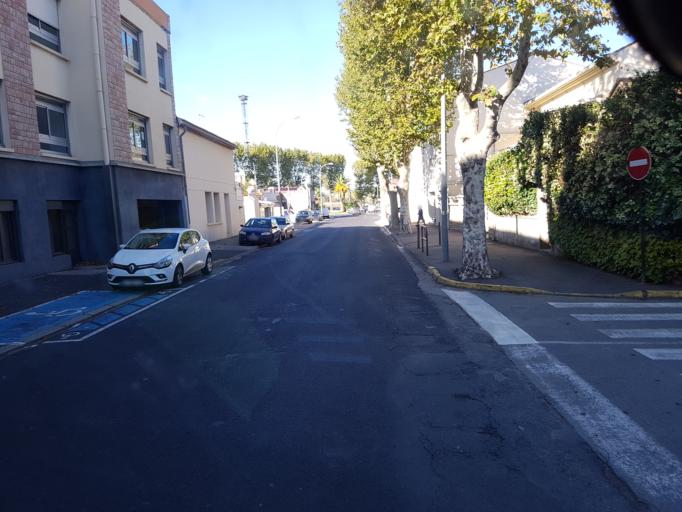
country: FR
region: Languedoc-Roussillon
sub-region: Departement de l'Aude
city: Narbonne
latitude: 43.1925
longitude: 3.0096
